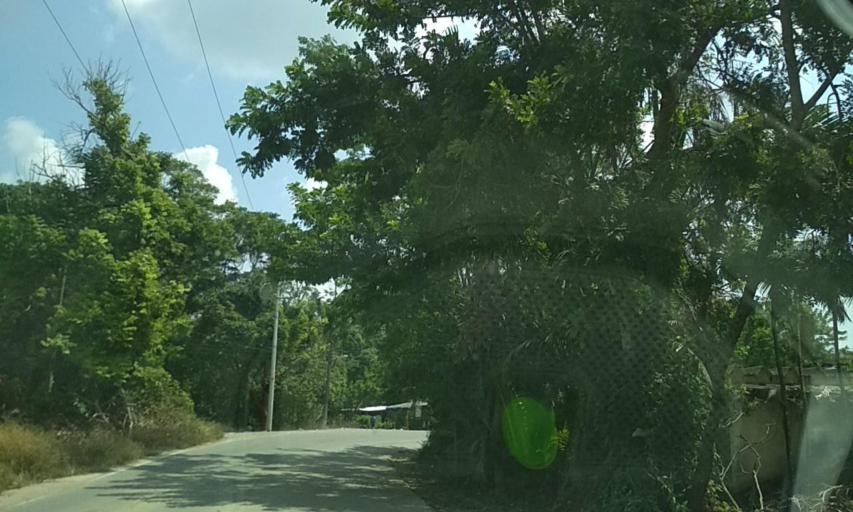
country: MX
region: Puebla
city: San Jose Acateno
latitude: 20.1752
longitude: -97.1125
